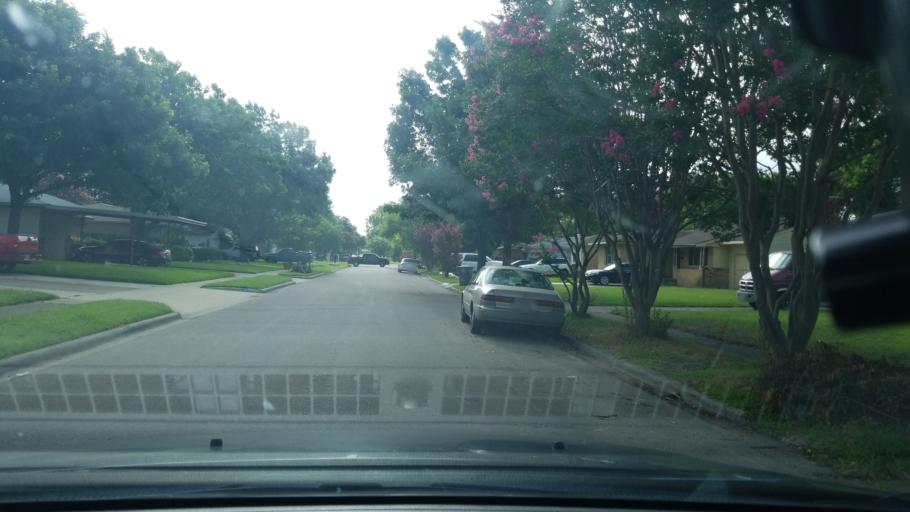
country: US
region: Texas
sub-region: Dallas County
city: Mesquite
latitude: 32.8197
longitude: -96.6700
